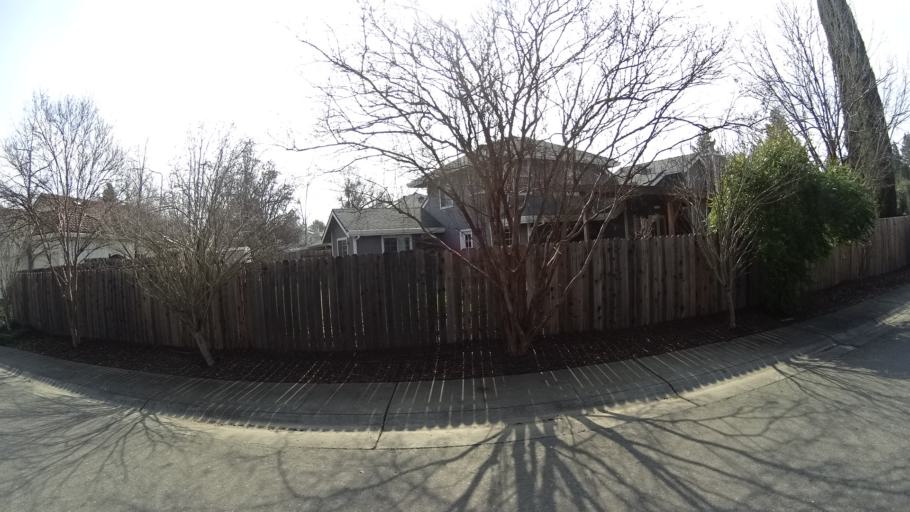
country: US
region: California
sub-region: Yolo County
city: Davis
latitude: 38.5740
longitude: -121.7546
